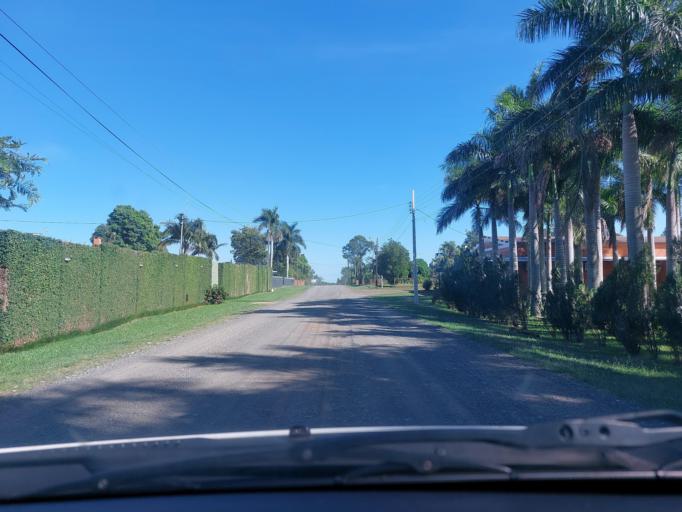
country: PY
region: San Pedro
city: Itacurubi del Rosario
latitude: -24.6125
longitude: -56.7947
